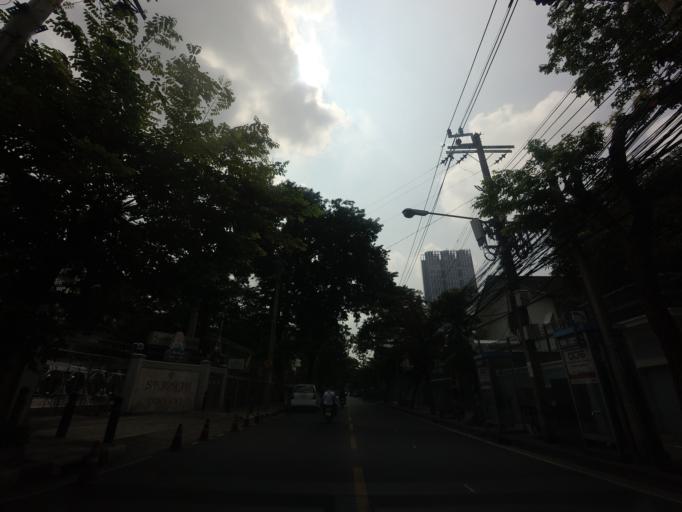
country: TH
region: Bangkok
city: Bang Rak
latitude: 13.7265
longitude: 100.5338
